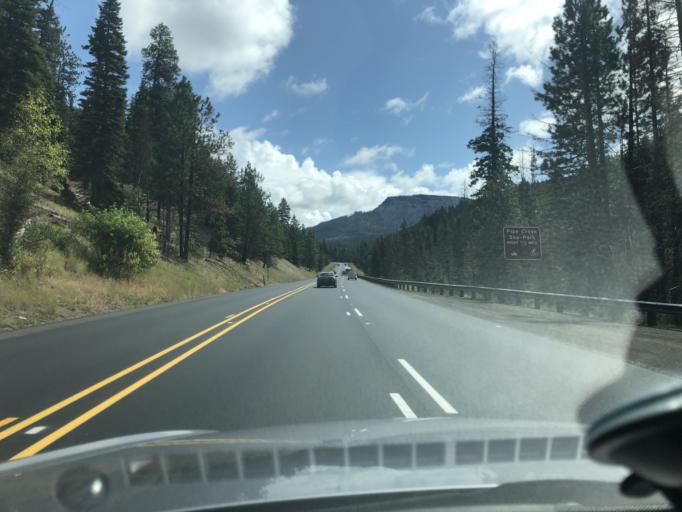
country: US
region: Washington
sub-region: Chelan County
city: Cashmere
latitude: 47.3343
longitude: -120.6213
